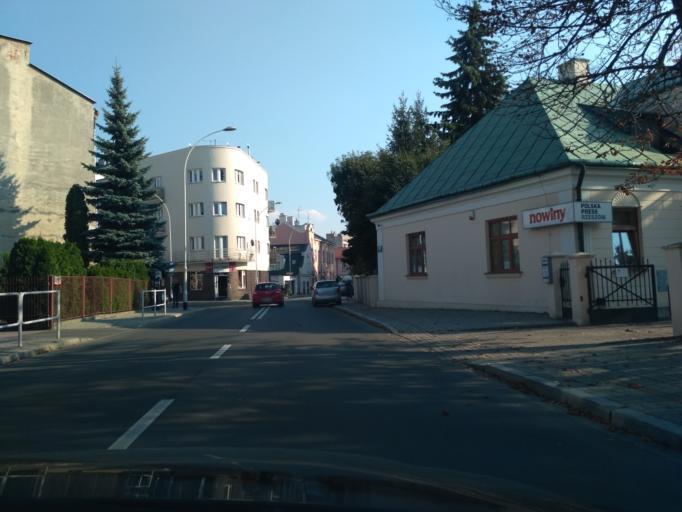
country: PL
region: Subcarpathian Voivodeship
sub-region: Rzeszow
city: Rzeszow
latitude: 50.0331
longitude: 21.9958
